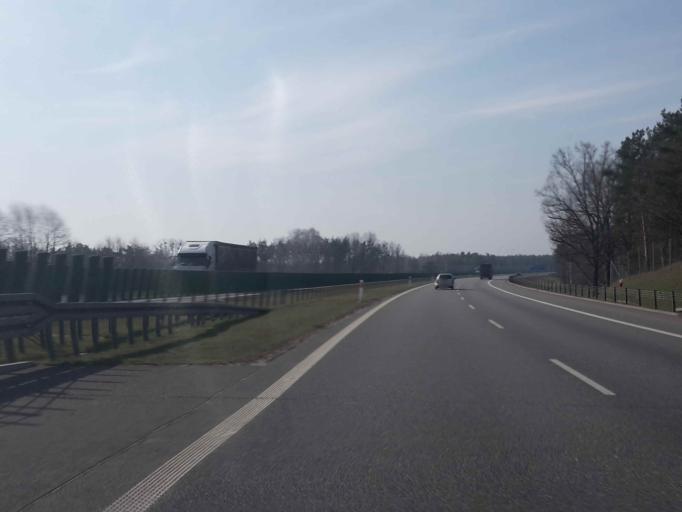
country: PL
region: Kujawsko-Pomorskie
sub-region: Powiat torunski
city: Lubicz Dolny
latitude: 52.9789
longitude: 18.7284
